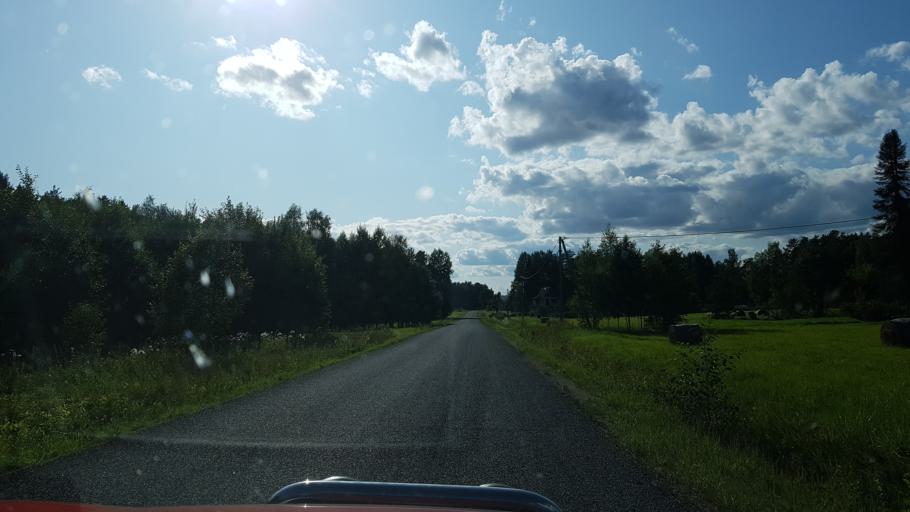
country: EE
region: Vorumaa
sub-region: Voru linn
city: Voru
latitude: 57.9265
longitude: 27.1054
